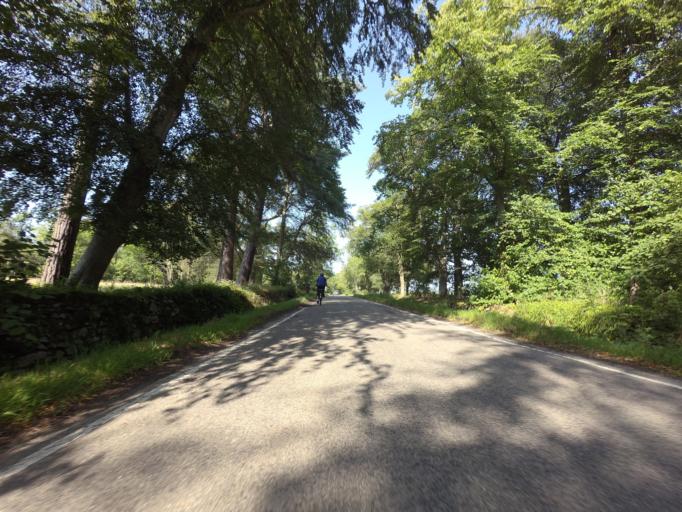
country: GB
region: Scotland
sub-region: Highland
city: Evanton
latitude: 57.6455
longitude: -4.3538
